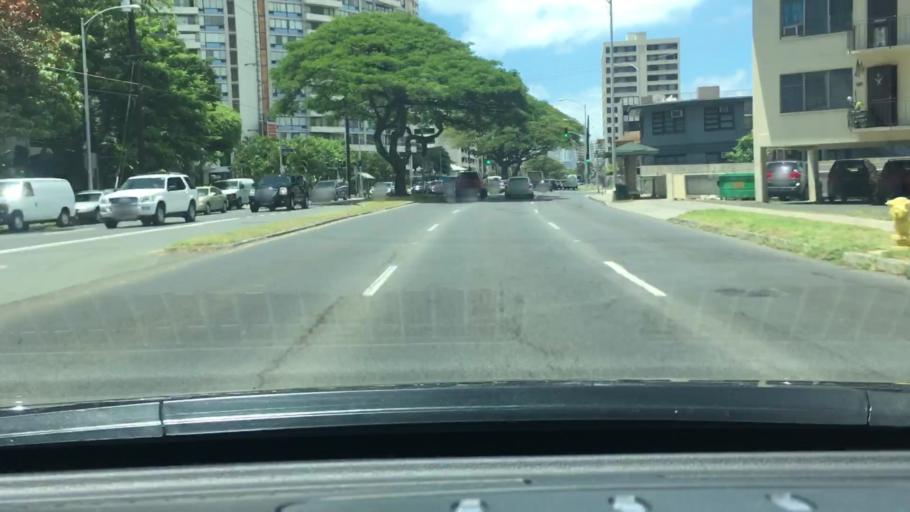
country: US
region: Hawaii
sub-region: Honolulu County
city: Honolulu
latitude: 21.2877
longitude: -157.8270
